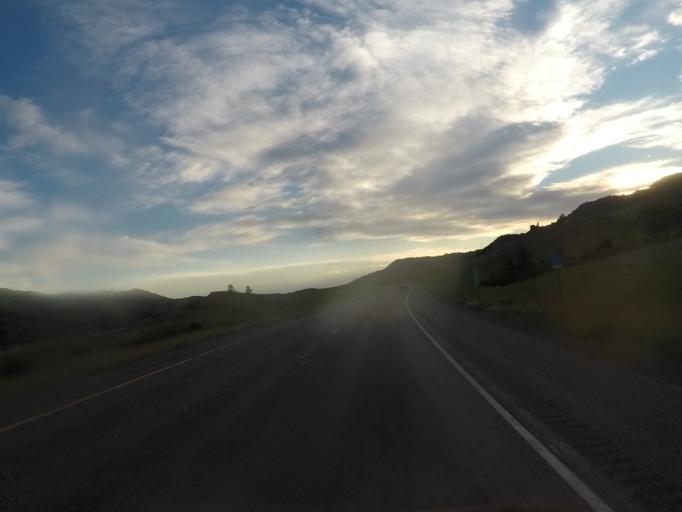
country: US
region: Montana
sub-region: Park County
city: Livingston
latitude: 45.6642
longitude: -110.6908
